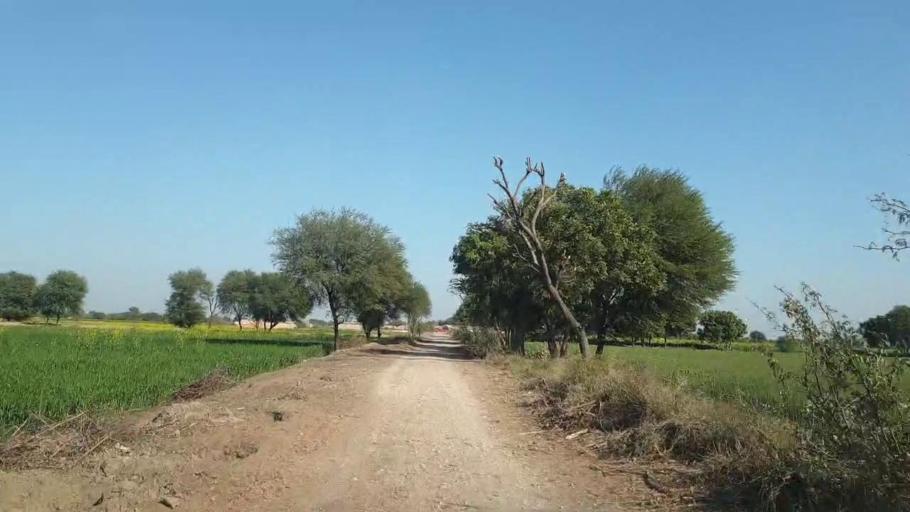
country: PK
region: Sindh
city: Tando Adam
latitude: 25.6721
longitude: 68.6852
